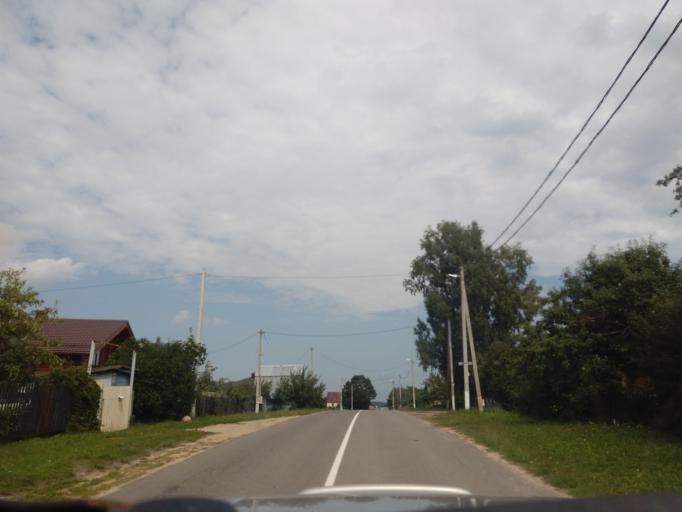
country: BY
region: Minsk
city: Khatsyezhyna
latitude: 53.9040
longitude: 27.2942
